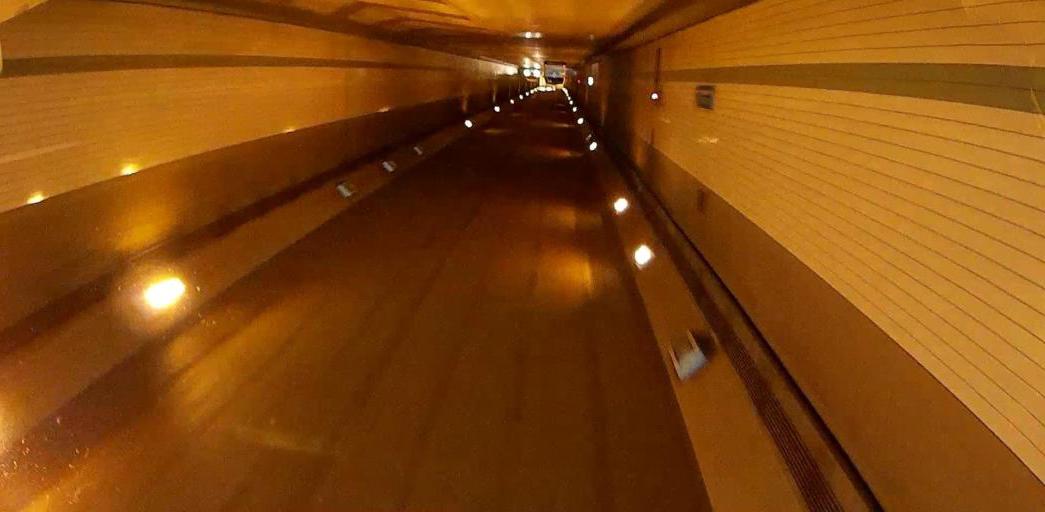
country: JP
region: Chiba
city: Narita
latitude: 35.7619
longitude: 140.3915
